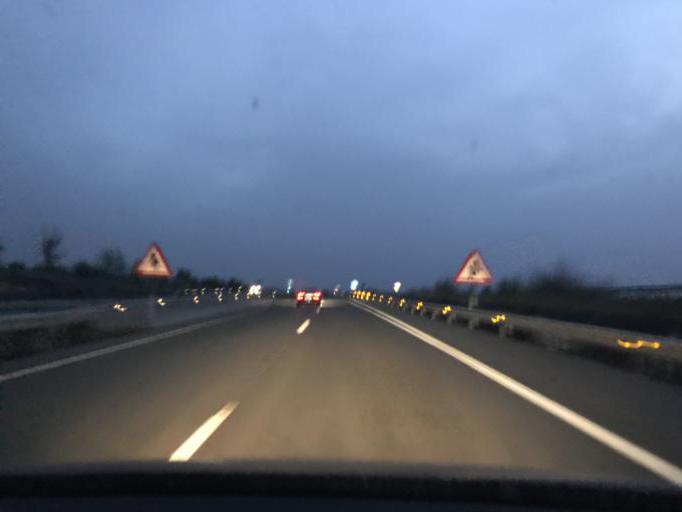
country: ES
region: Andalusia
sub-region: Provincia de Granada
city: Gor
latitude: 37.3992
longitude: -2.9506
